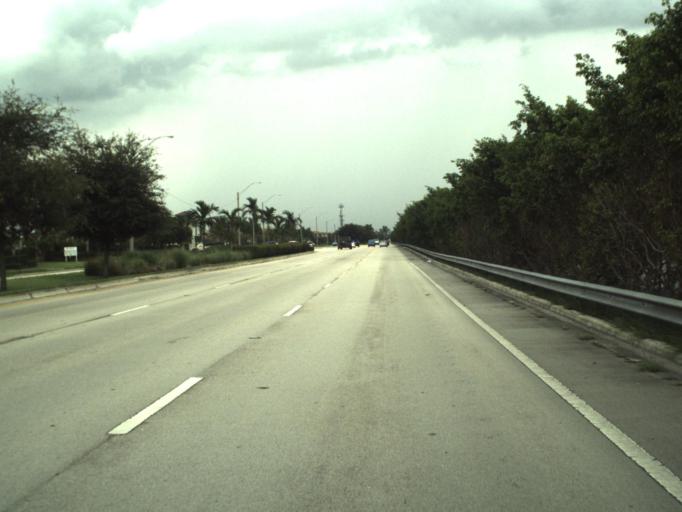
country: US
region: Florida
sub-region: Broward County
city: Cooper City
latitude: 26.0307
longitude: -80.2589
